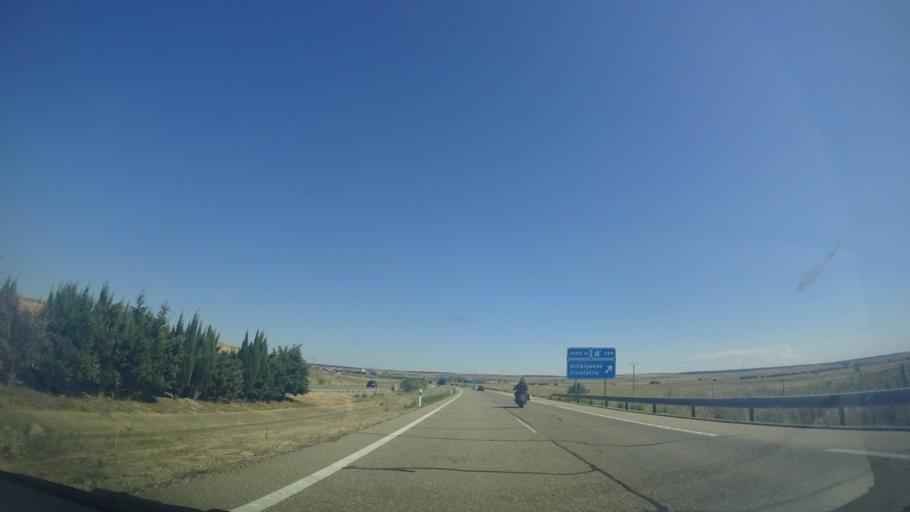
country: ES
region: Castille and Leon
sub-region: Provincia de Zamora
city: Cerecinos de Campos
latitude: 41.8790
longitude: -5.4524
